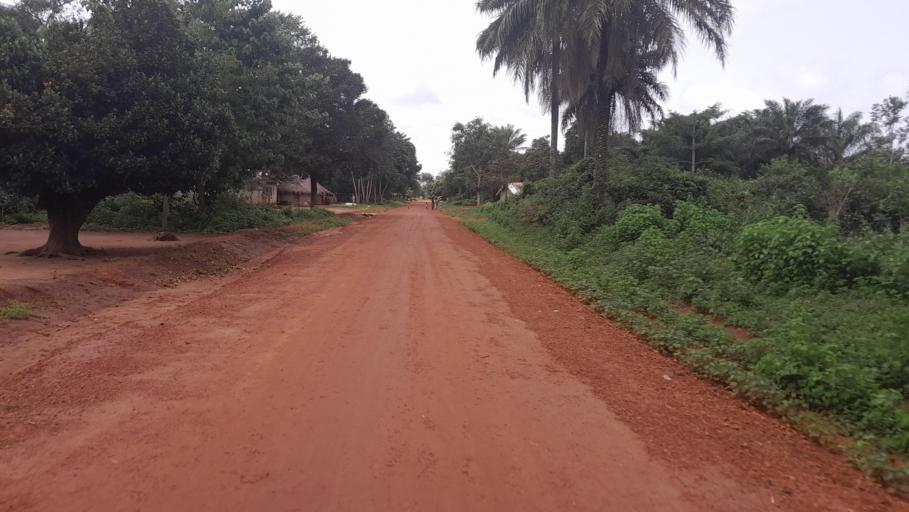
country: GN
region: Boke
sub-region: Boffa
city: Boffa
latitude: 10.0105
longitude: -13.8871
